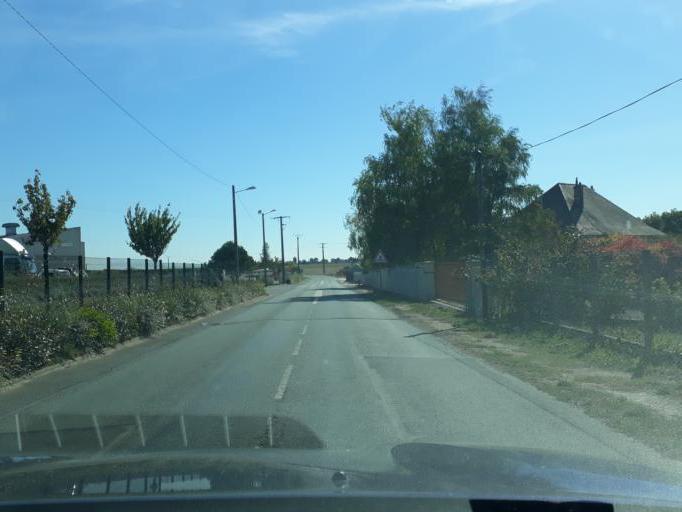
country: FR
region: Centre
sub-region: Departement du Loir-et-Cher
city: Ouzouer-le-Marche
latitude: 47.8852
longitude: 1.5494
